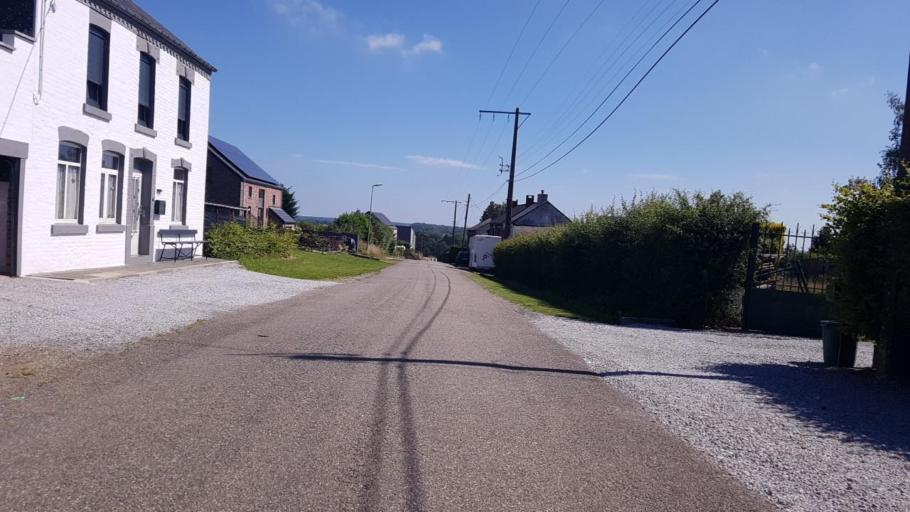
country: BE
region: Wallonia
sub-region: Province du Hainaut
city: Momignies
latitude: 50.0394
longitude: 4.2016
